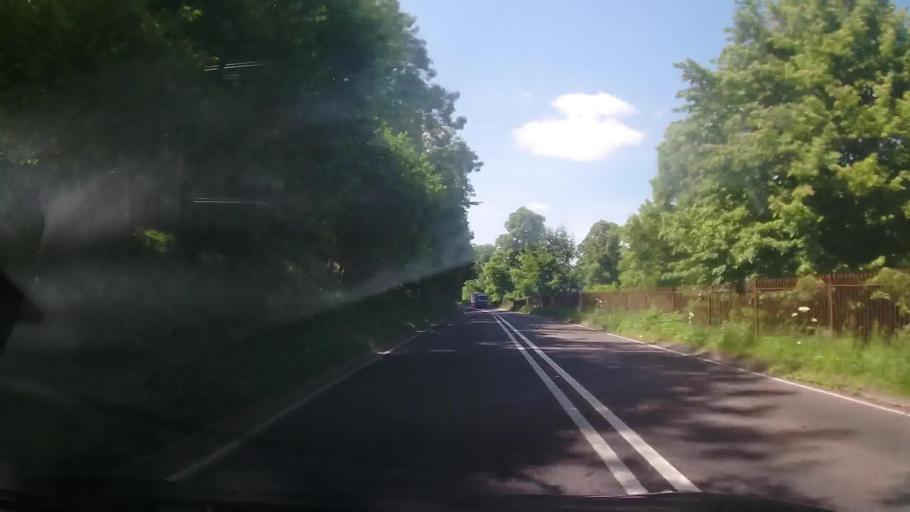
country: GB
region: England
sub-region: Herefordshire
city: Kimbolton
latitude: 52.2701
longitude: -2.7121
